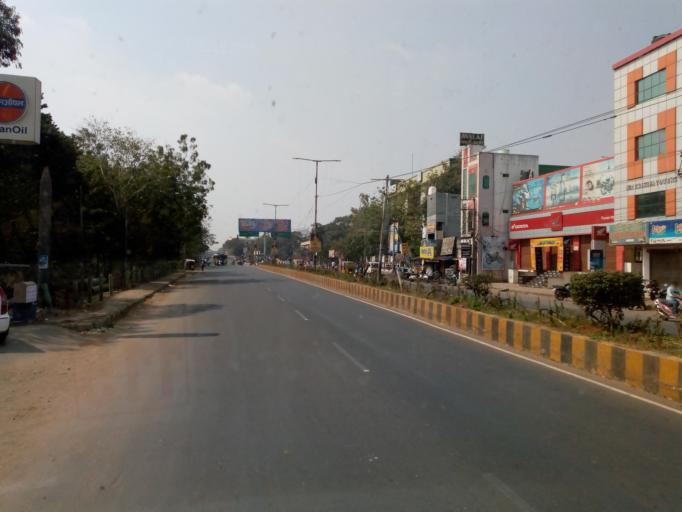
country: IN
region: Andhra Pradesh
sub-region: West Godavari
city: Eluru
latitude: 16.7089
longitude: 81.1030
